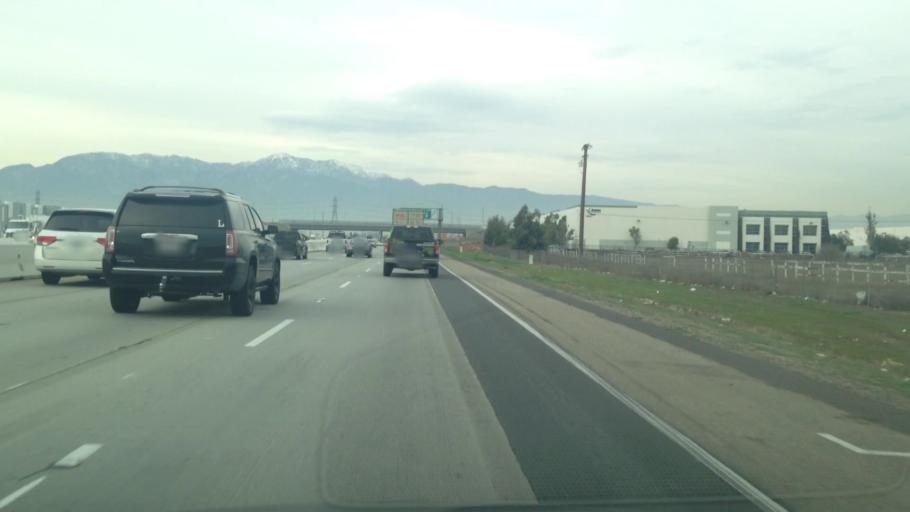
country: US
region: California
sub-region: Riverside County
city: Mira Loma
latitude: 33.9966
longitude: -117.5494
